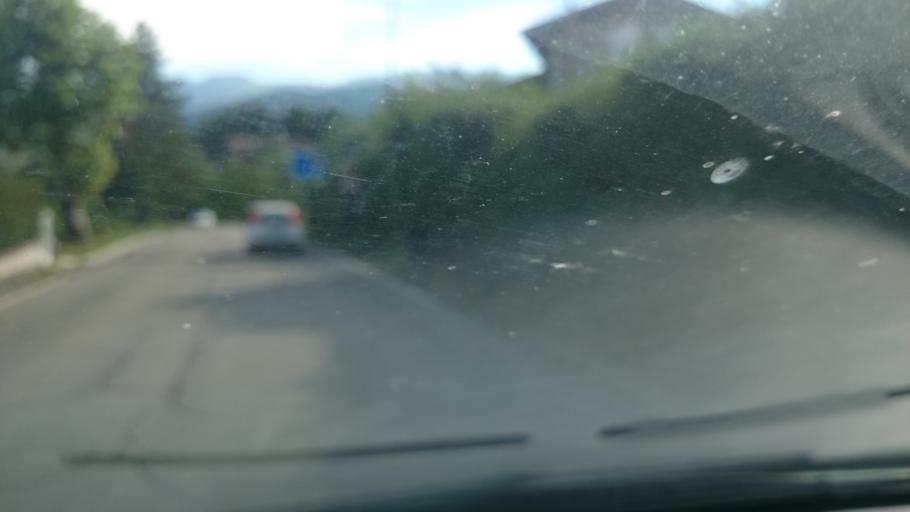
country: IT
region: Emilia-Romagna
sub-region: Provincia di Reggio Emilia
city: Villa Minozzo
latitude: 44.3611
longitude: 10.4659
